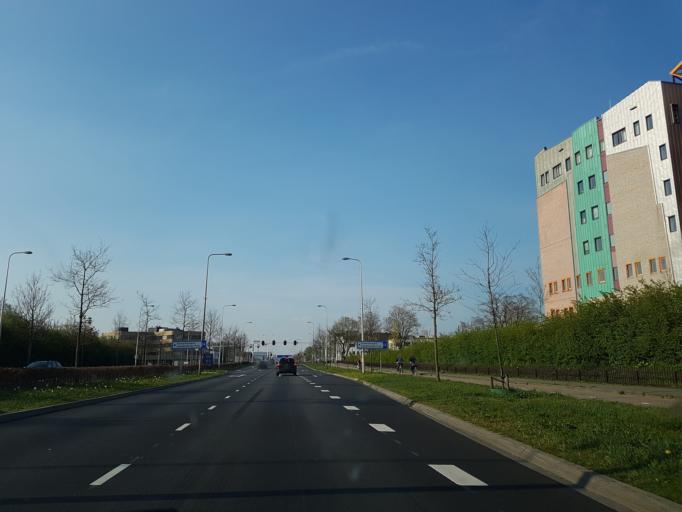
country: NL
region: Overijssel
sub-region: Gemeente Zwolle
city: Zwolle
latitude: 52.5124
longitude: 6.1209
